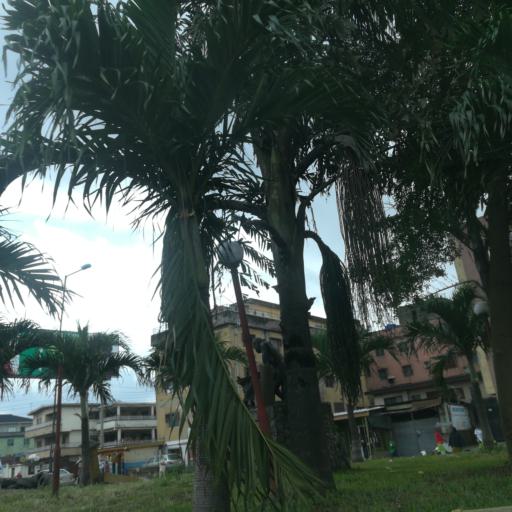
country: NG
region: Lagos
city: Mushin
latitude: 6.5312
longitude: 3.3409
